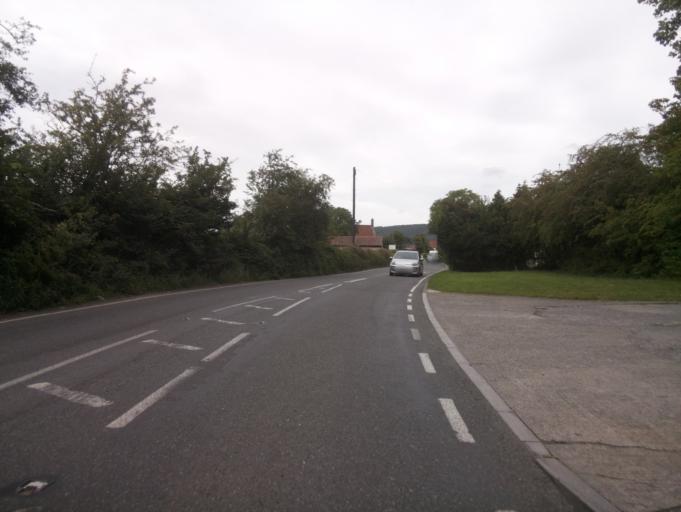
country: GB
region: England
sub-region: North Somerset
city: Churchill
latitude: 51.3505
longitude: -2.7846
